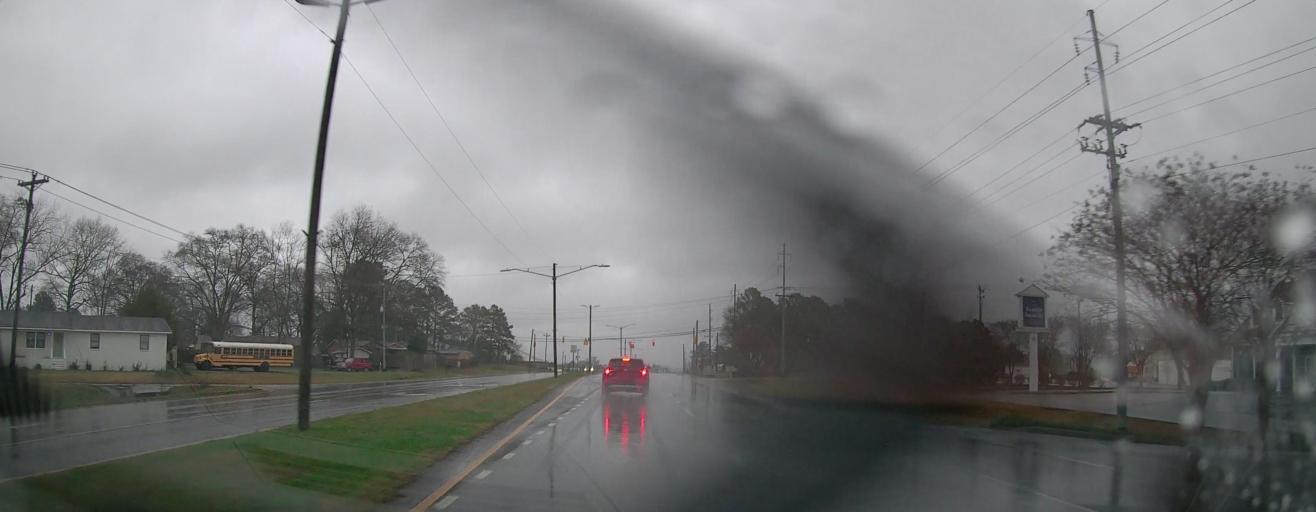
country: US
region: Alabama
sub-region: Morgan County
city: Hartselle
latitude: 34.4324
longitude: -86.9363
